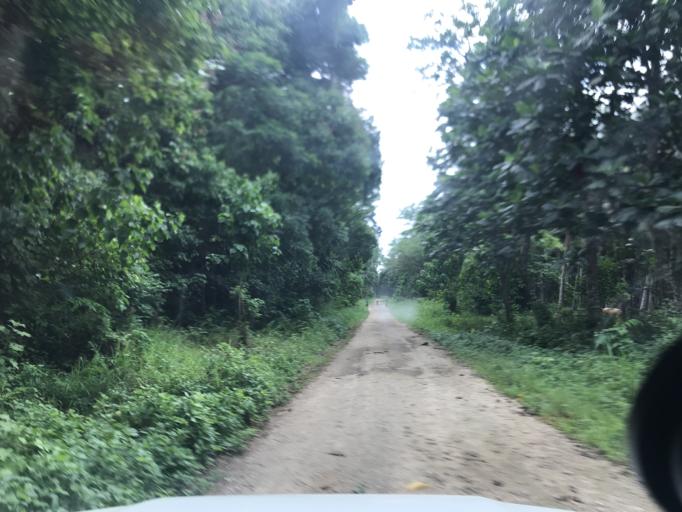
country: VU
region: Sanma
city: Port-Olry
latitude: -15.1693
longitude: 166.9494
